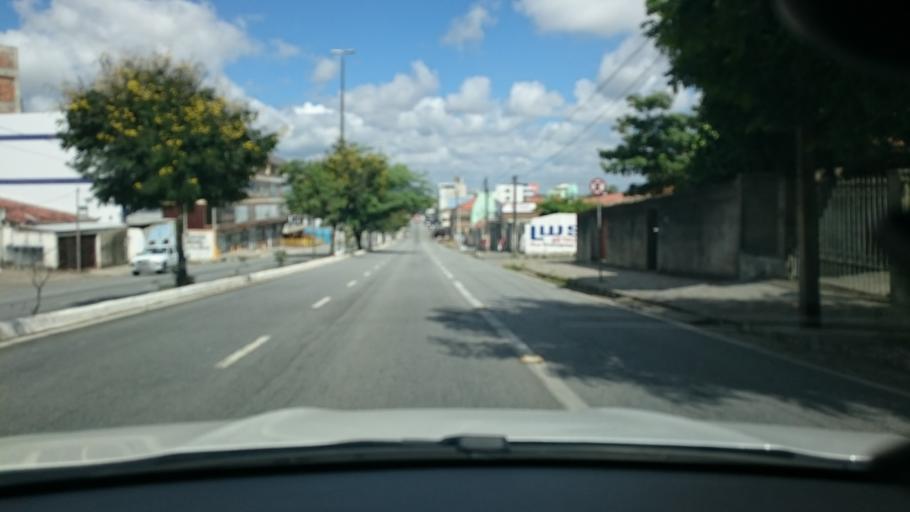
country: BR
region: Paraiba
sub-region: Campina Grande
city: Campina Grande
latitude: -7.2278
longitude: -35.9019
